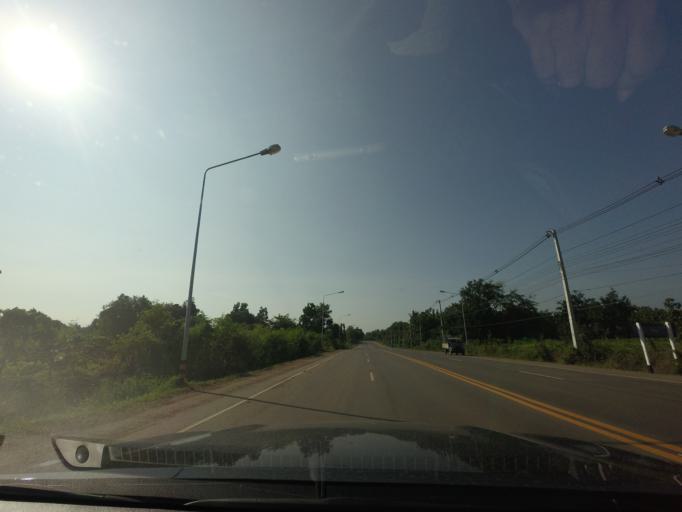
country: TH
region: Phetchabun
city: Lom Sak
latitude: 16.8137
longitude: 101.1821
